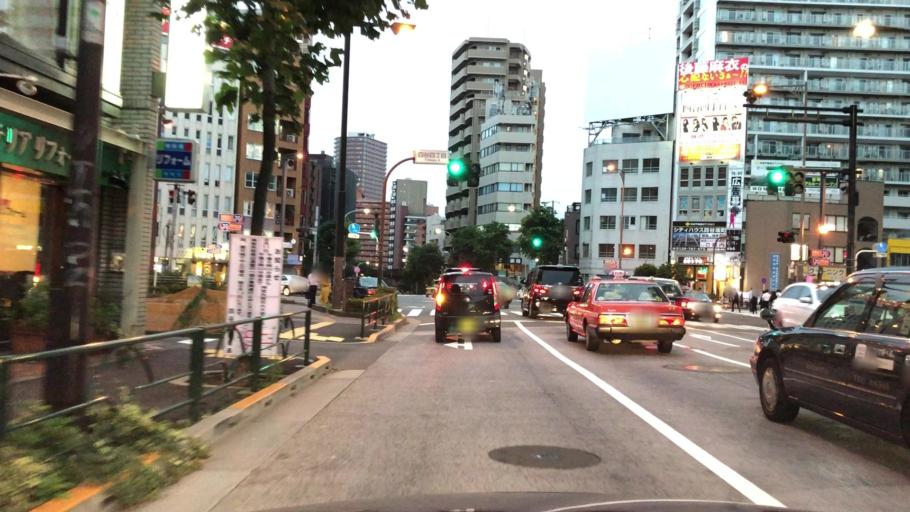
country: JP
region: Tokyo
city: Tokyo
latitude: 35.6870
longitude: 139.7159
